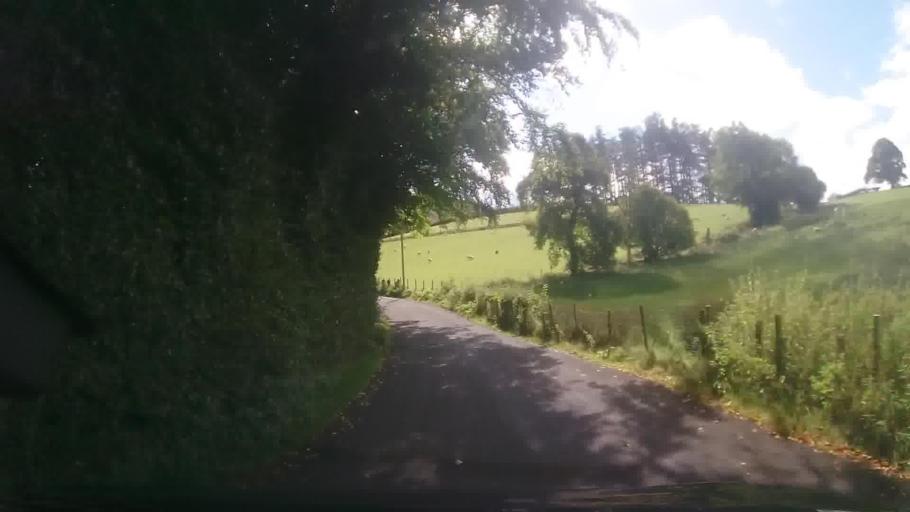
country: GB
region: Wales
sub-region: Gwynedd
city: Bala
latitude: 52.7628
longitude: -3.6223
